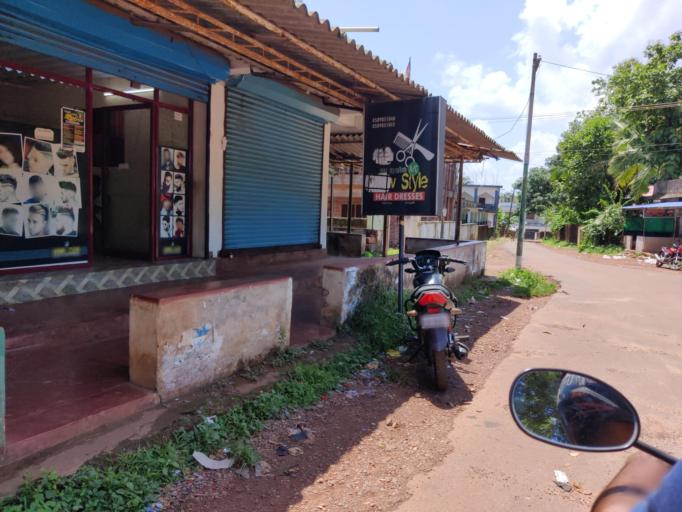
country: IN
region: Kerala
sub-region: Kasaragod District
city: Kasaragod
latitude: 12.4044
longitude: 75.0474
